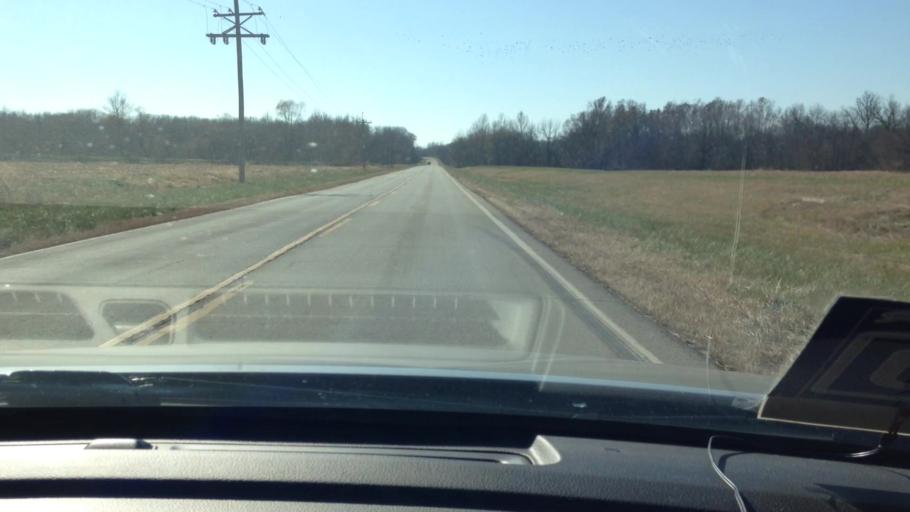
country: US
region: Missouri
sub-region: Platte County
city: Platte City
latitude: 39.4868
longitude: -94.8058
